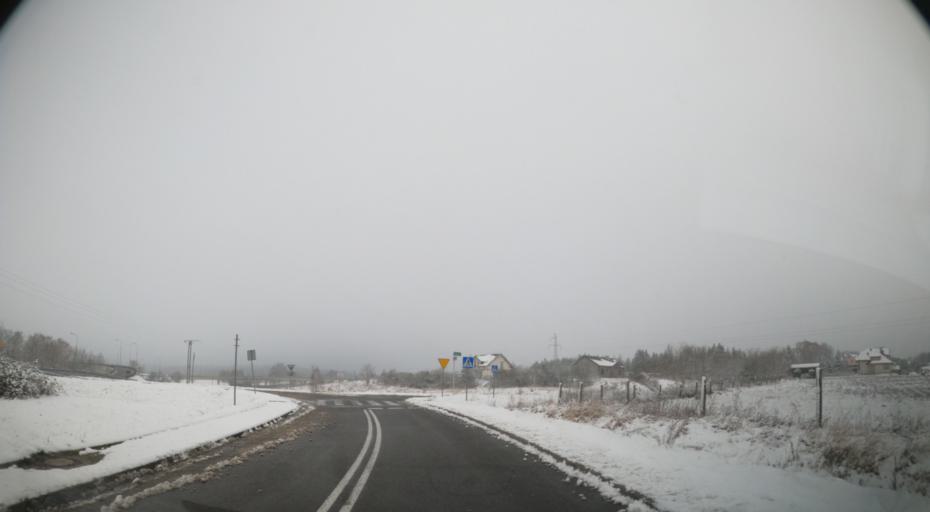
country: PL
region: West Pomeranian Voivodeship
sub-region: Szczecin
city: Szczecin
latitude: 53.3411
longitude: 14.5704
